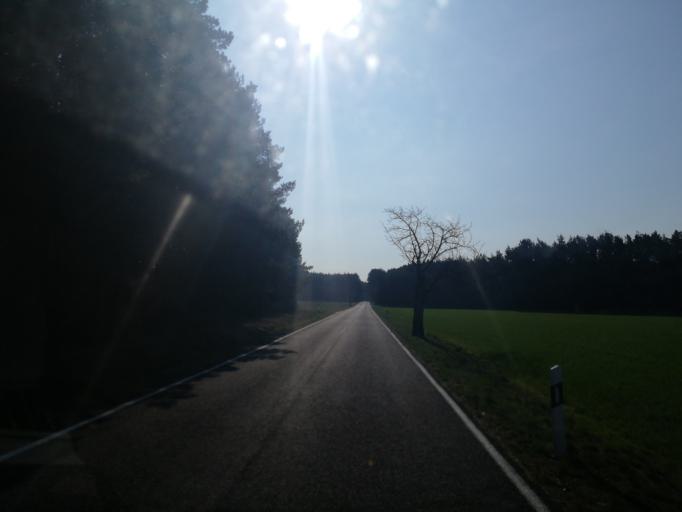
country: DE
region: Brandenburg
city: Sonnewalde
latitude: 51.7762
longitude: 13.6346
